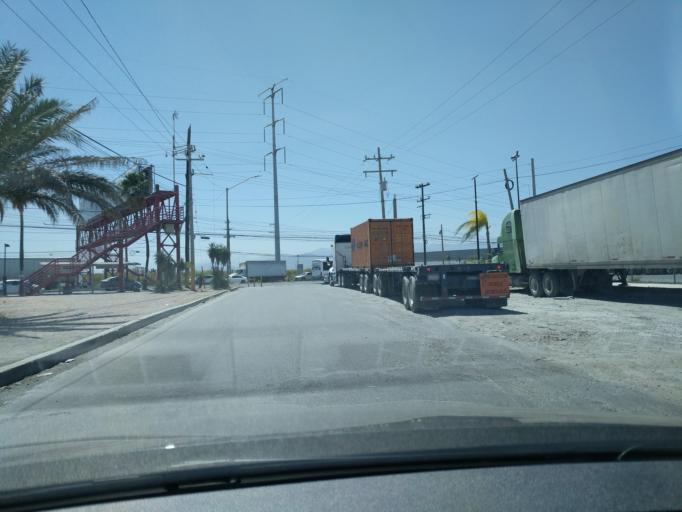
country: MX
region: Nuevo Leon
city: Apodaca
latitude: 25.7855
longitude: -100.1596
